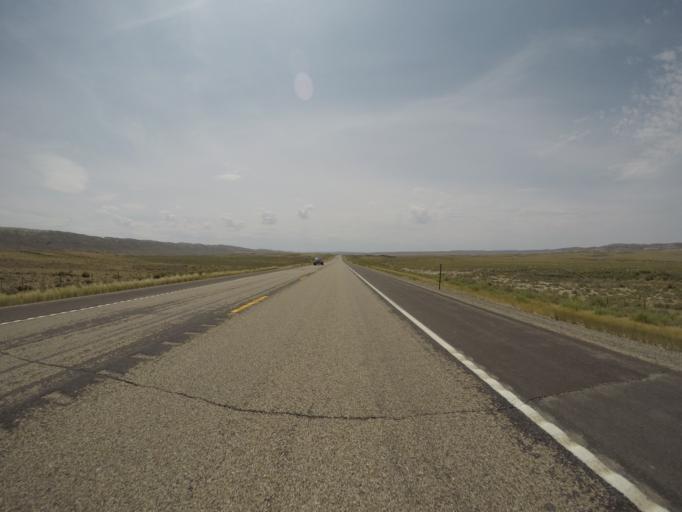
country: US
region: Wyoming
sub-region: Lincoln County
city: Kemmerer
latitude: 41.6691
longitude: -110.5693
